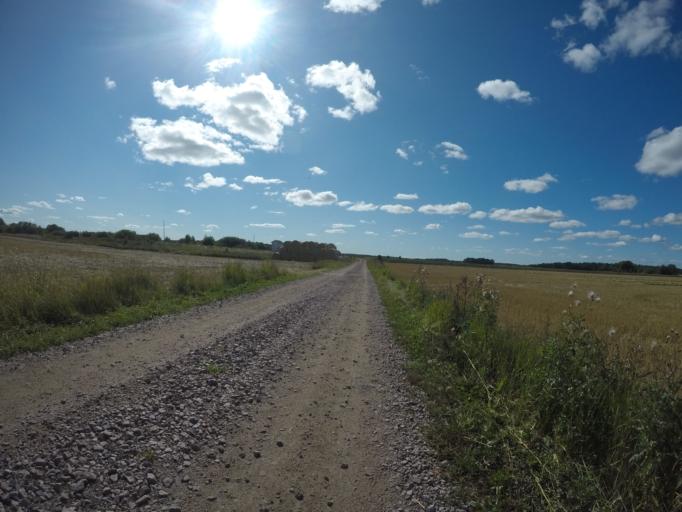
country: SE
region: Vaestmanland
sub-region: Hallstahammars Kommun
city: Kolback
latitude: 59.5113
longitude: 16.2401
